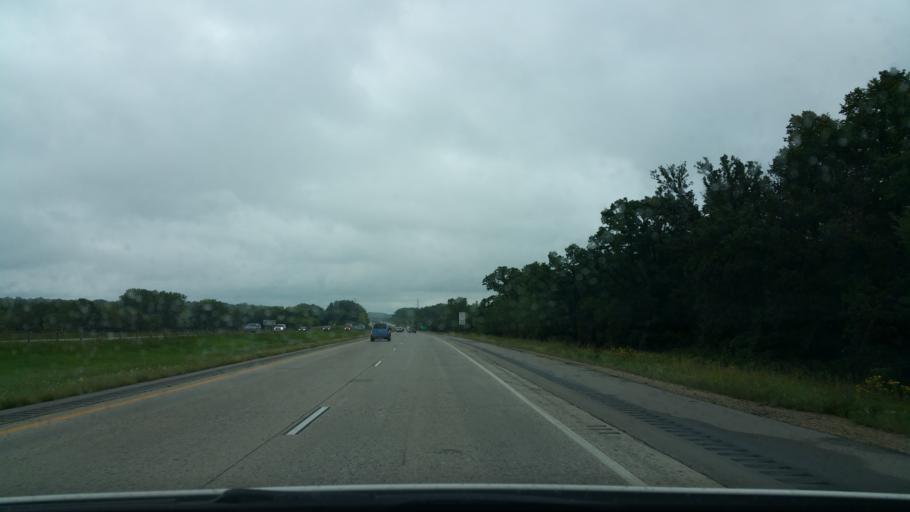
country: US
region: Minnesota
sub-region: Scott County
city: Elko New Market
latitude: 44.5799
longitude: -93.2977
